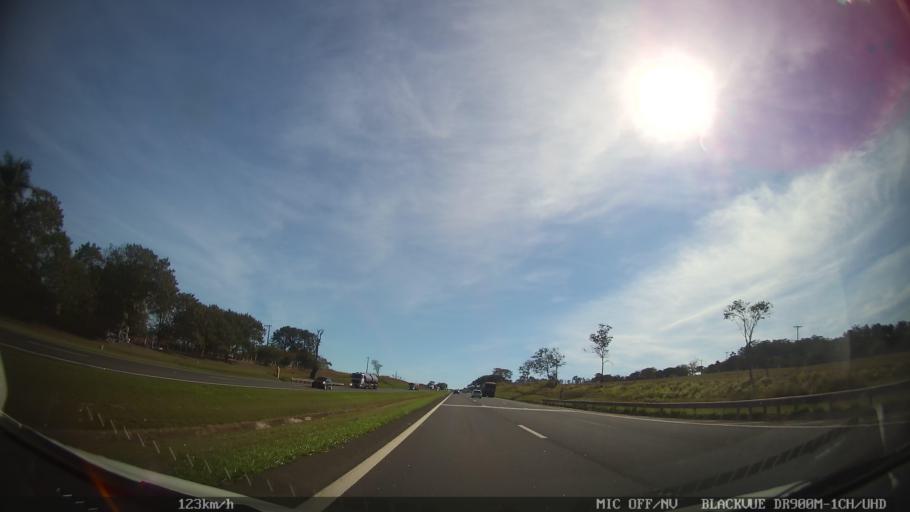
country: BR
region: Sao Paulo
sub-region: Pirassununga
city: Pirassununga
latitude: -22.0470
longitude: -47.4301
